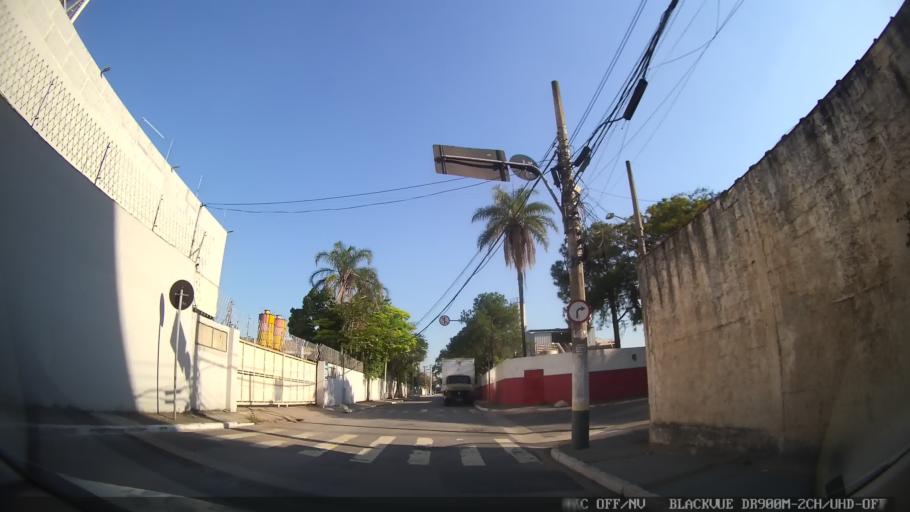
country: BR
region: Sao Paulo
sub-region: Sao Paulo
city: Sao Paulo
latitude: -23.5086
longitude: -46.6690
